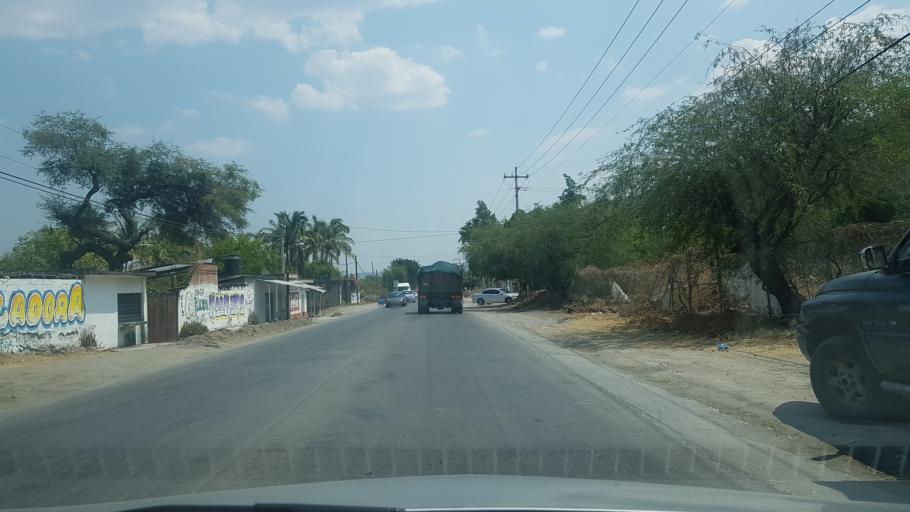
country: MX
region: Morelos
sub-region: Tlaltizapan de Zapata
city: Colonia Palo Prieto (Chipitongo)
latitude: 18.7175
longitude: -99.1198
